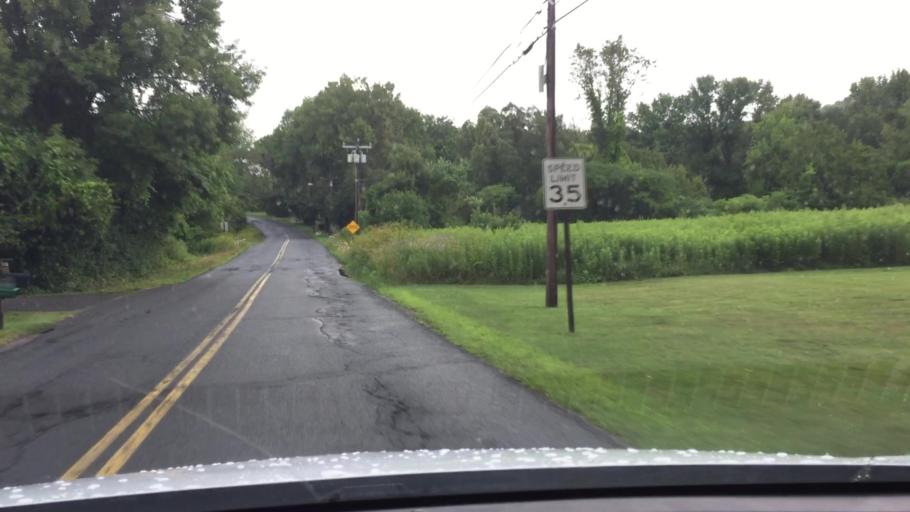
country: US
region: Massachusetts
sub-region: Berkshire County
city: Dalton
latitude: 42.4261
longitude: -73.1938
